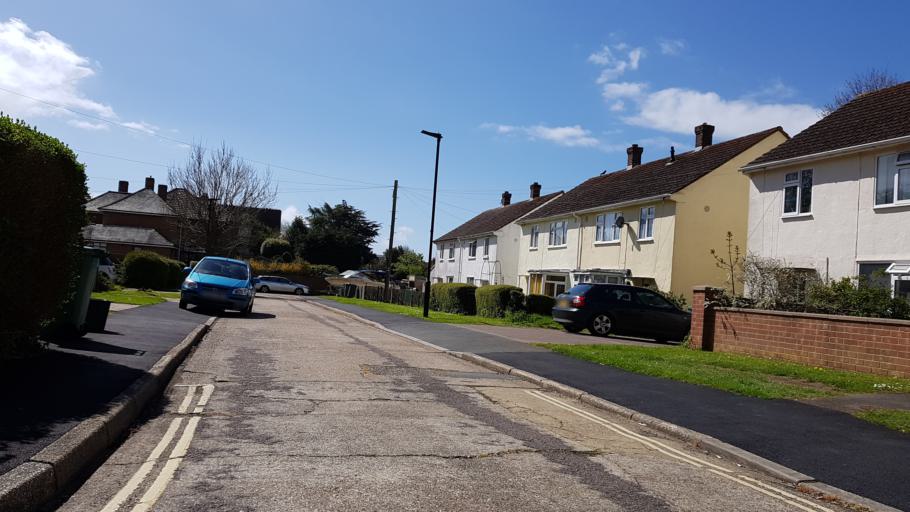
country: GB
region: England
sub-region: Isle of Wight
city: East Cowes
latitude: 50.7523
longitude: -1.2780
